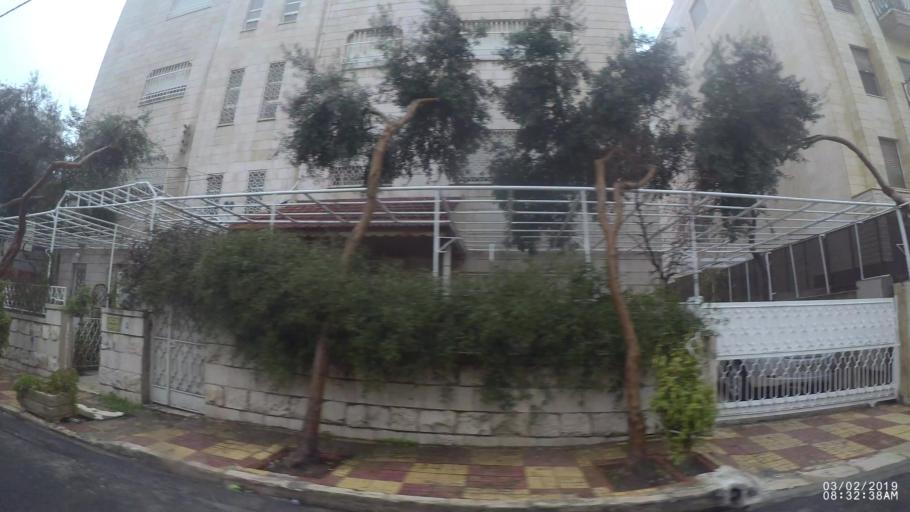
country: JO
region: Amman
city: Wadi as Sir
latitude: 31.9625
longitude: 35.8719
